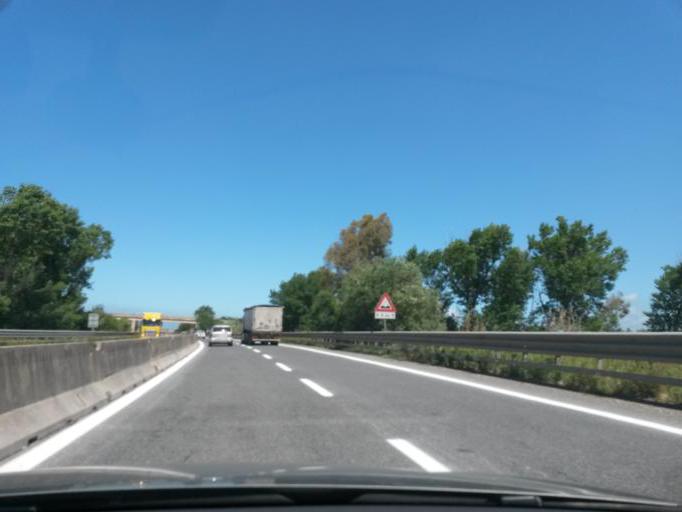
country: IT
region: Tuscany
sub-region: Provincia di Livorno
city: Cecina
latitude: 43.3037
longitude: 10.5465
